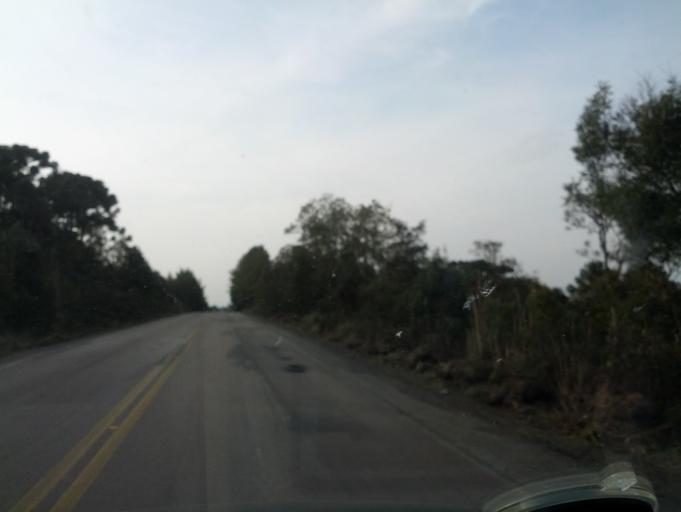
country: BR
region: Santa Catarina
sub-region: Otacilio Costa
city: Otacilio Costa
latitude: -27.3502
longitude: -50.1302
